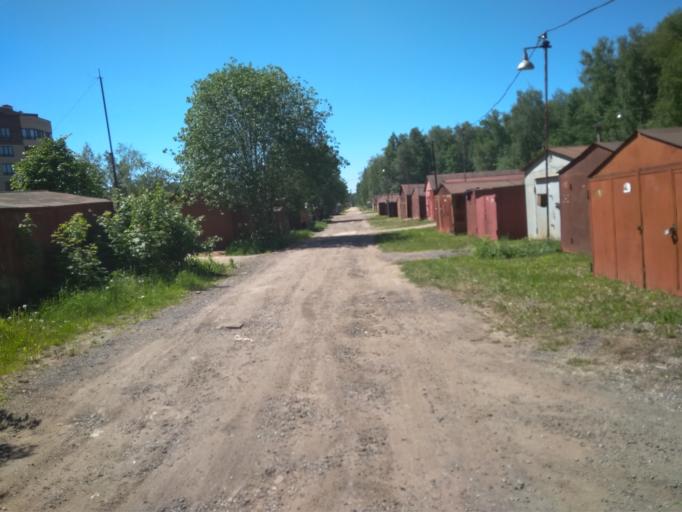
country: RU
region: Moskovskaya
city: Troitsk
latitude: 55.4693
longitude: 37.2880
